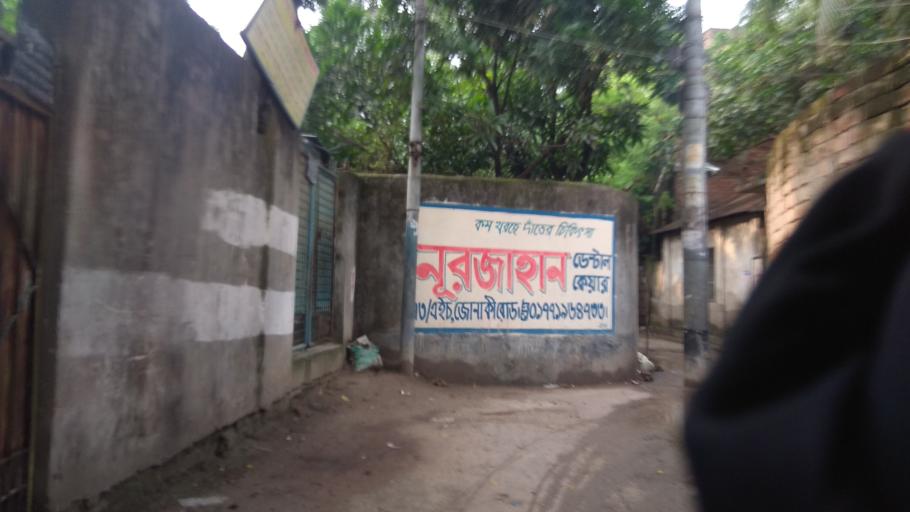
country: BD
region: Dhaka
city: Azimpur
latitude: 23.7946
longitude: 90.3628
